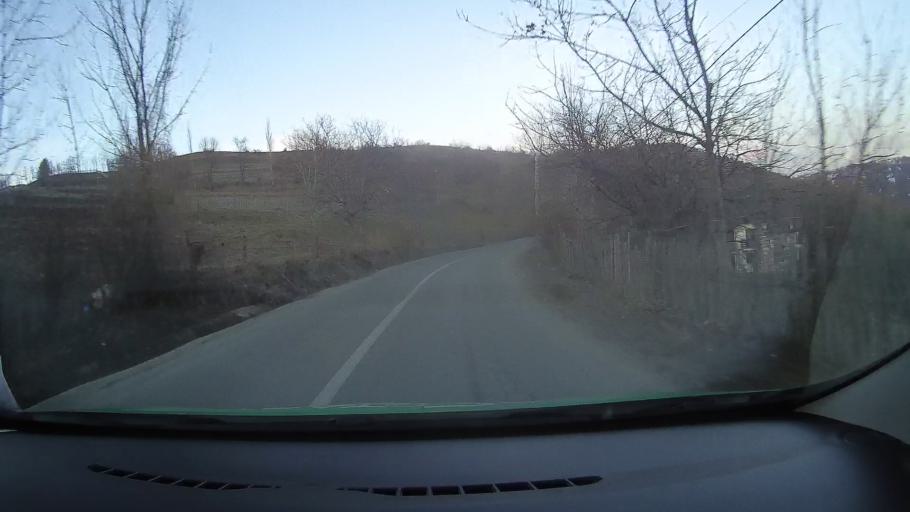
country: RO
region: Prahova
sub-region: Comuna Comarnic
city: Comarnic
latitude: 45.2574
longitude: 25.6472
